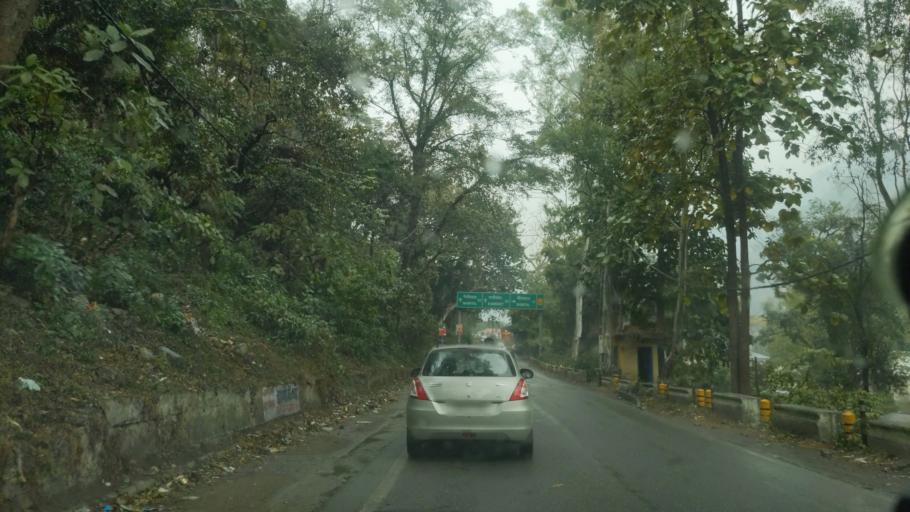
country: IN
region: Uttarakhand
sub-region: Naini Tal
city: Bhim Tal
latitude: 29.2889
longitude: 79.5468
